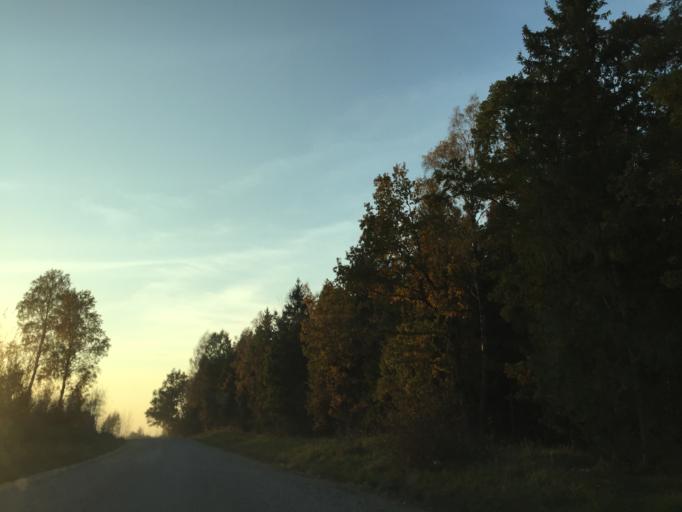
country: LV
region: Priekule
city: Priekule
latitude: 56.4812
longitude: 21.7049
